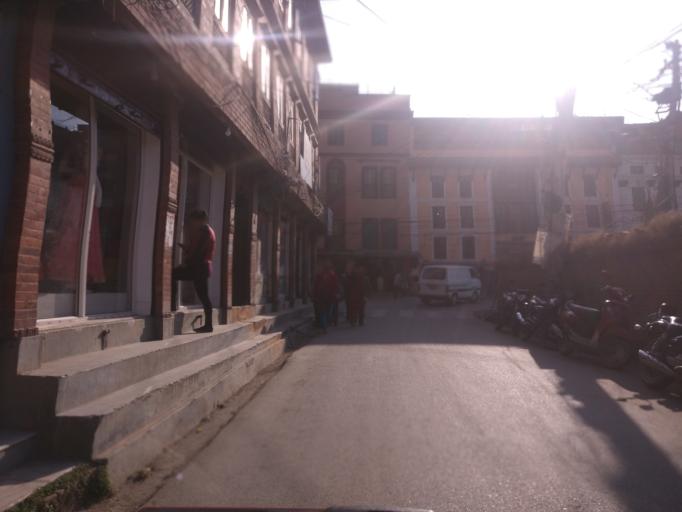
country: NP
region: Central Region
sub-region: Bagmati Zone
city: Patan
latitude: 27.6760
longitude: 85.3187
